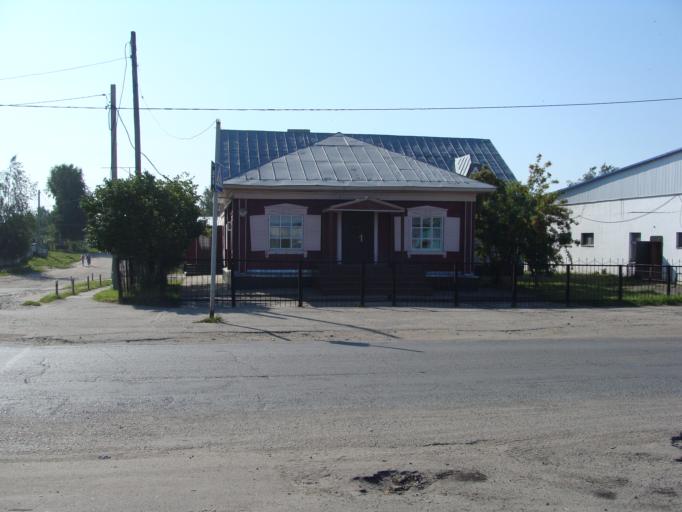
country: RU
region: Altai Krai
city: Vlasikha
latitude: 53.2966
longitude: 83.5822
